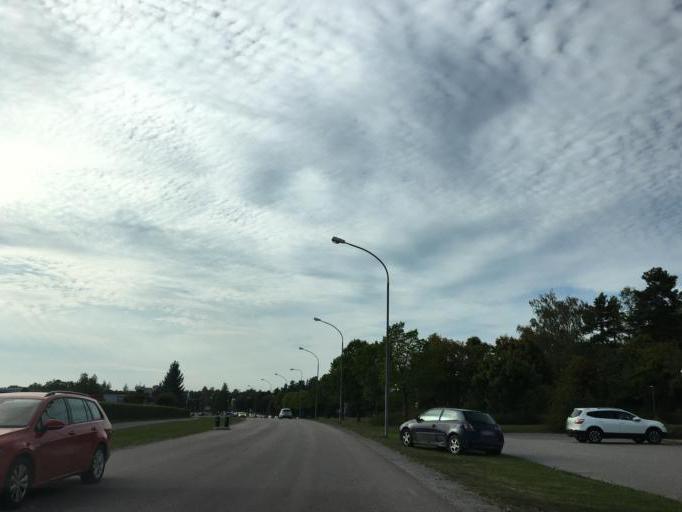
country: SE
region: Soedermanland
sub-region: Eskilstuna Kommun
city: Torshalla
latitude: 59.4181
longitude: 16.4877
